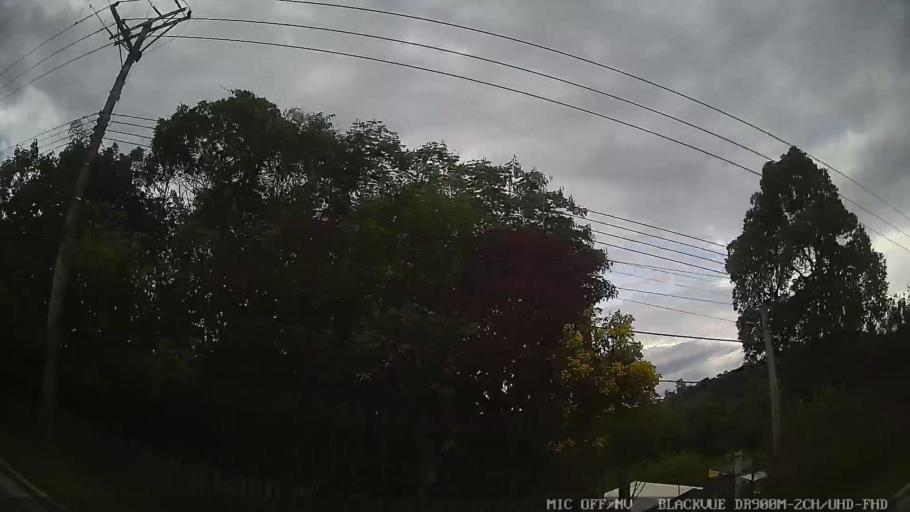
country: BR
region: Sao Paulo
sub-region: Biritiba-Mirim
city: Biritiba Mirim
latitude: -23.5660
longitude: -46.0176
